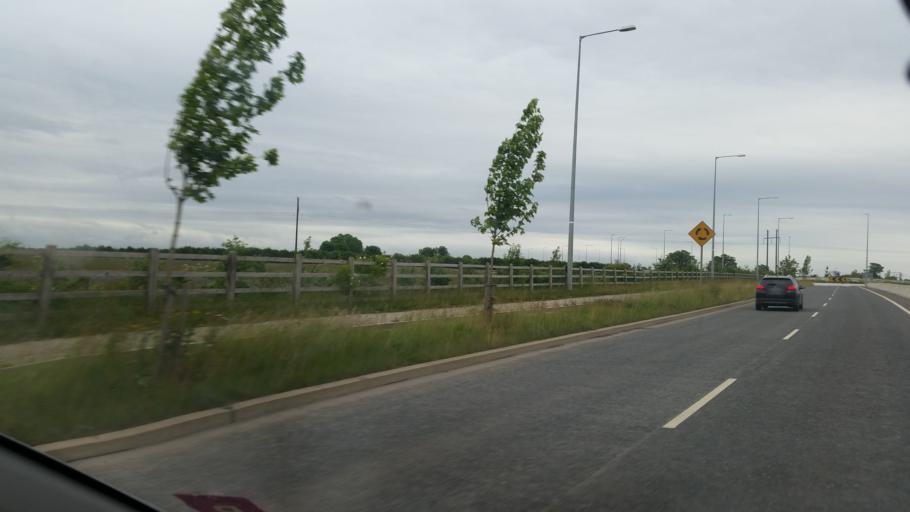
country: IE
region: Leinster
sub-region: Fingal County
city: Blanchardstown
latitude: 53.4216
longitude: -6.3737
